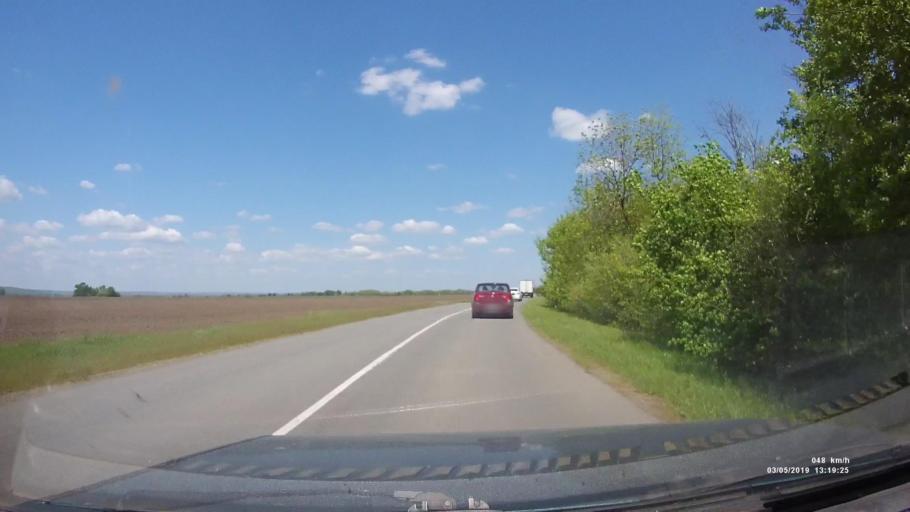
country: RU
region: Rostov
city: Semikarakorsk
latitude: 47.5375
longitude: 40.7481
